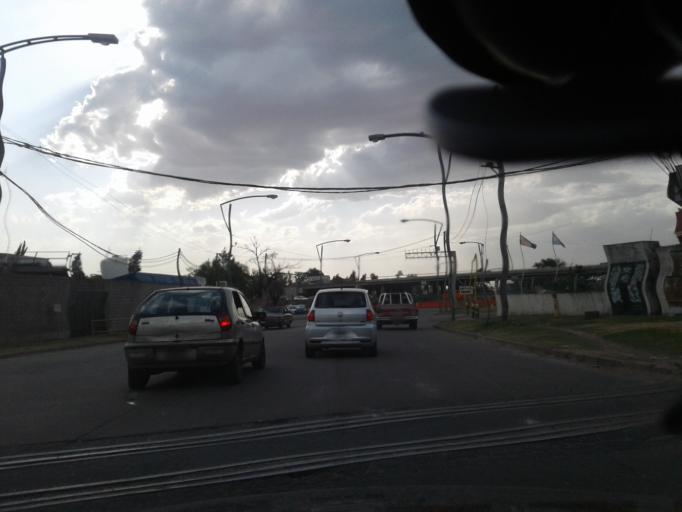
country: AR
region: Santa Fe
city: Granadero Baigorria
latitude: -32.8938
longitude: -60.7182
